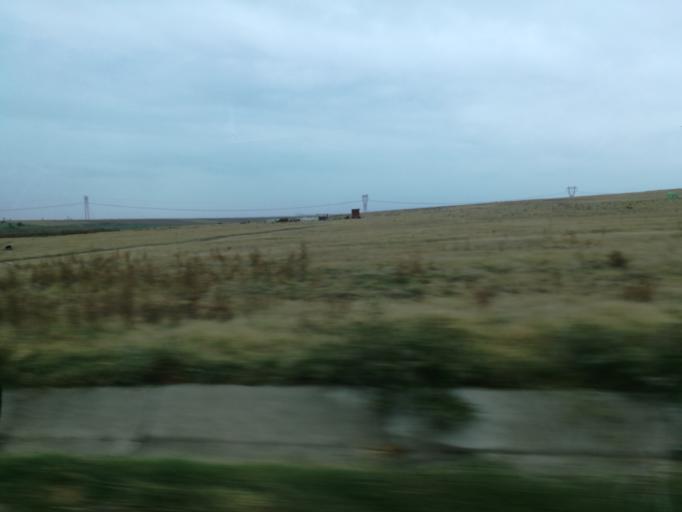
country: RO
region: Constanta
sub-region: Comuna Cogealac
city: Tariverde
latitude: 44.5523
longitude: 28.5992
